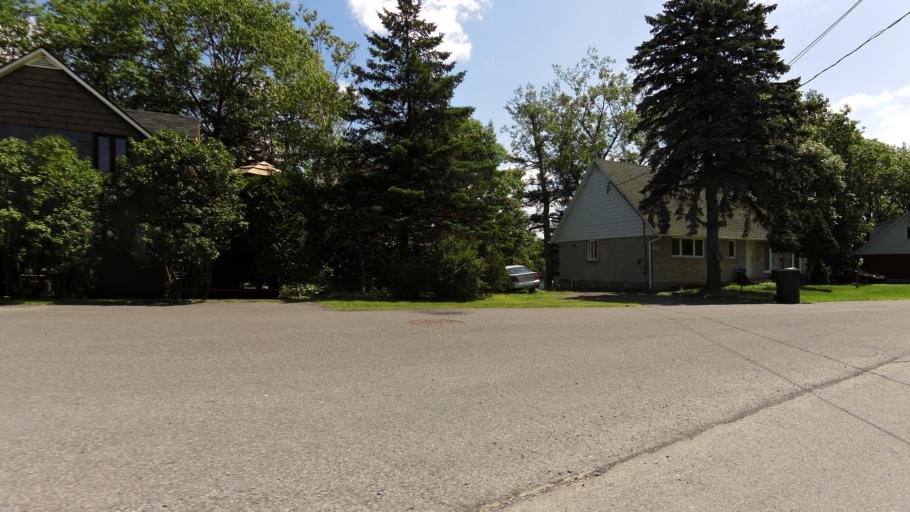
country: CA
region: Quebec
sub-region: Monteregie
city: Richelieu
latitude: 45.4325
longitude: -73.2500
